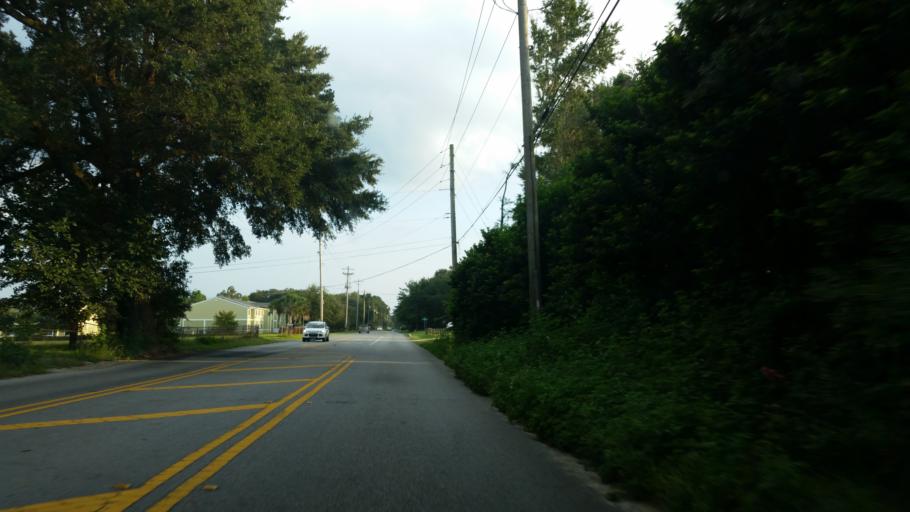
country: US
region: Florida
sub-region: Santa Rosa County
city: Pace
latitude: 30.6001
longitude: -87.1155
